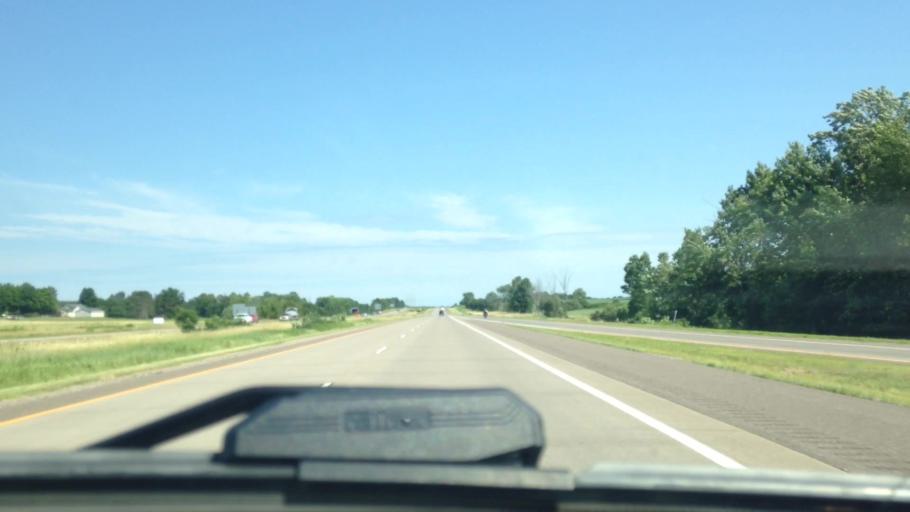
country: US
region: Wisconsin
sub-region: Barron County
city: Rice Lake
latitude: 45.4757
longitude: -91.7593
